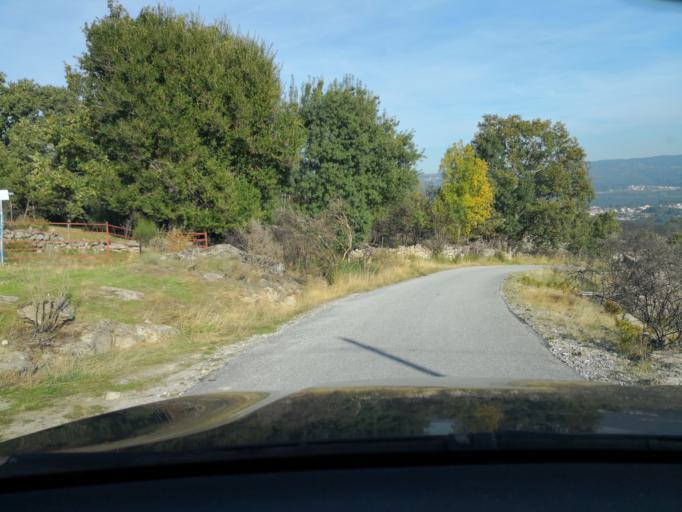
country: PT
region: Vila Real
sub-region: Vila Real
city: Vila Real
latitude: 41.3420
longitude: -7.7555
